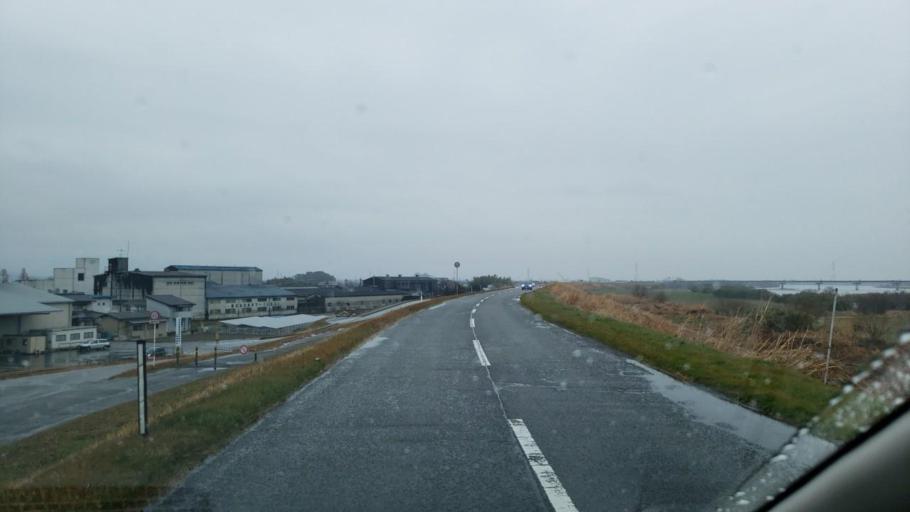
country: JP
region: Tokushima
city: Ishii
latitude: 34.1045
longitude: 134.4228
